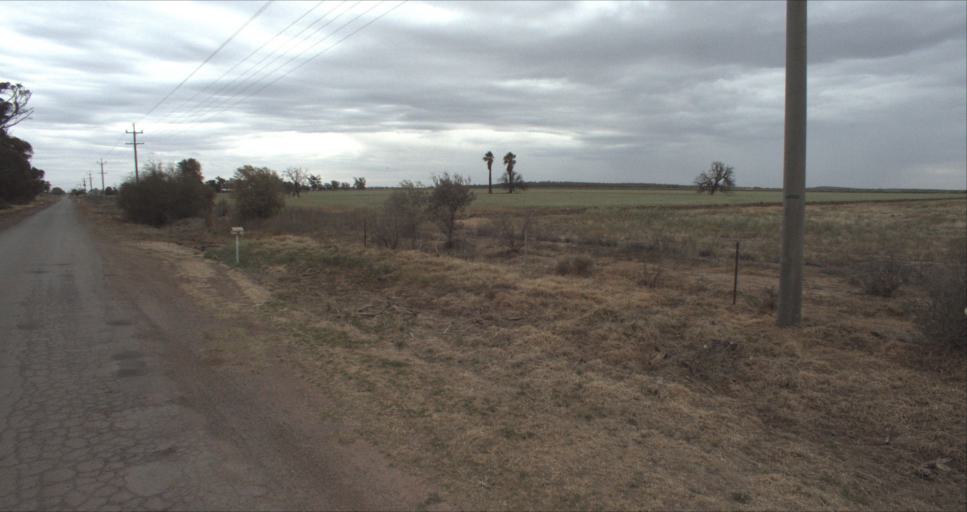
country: AU
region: New South Wales
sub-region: Leeton
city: Leeton
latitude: -34.4040
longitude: 146.3416
